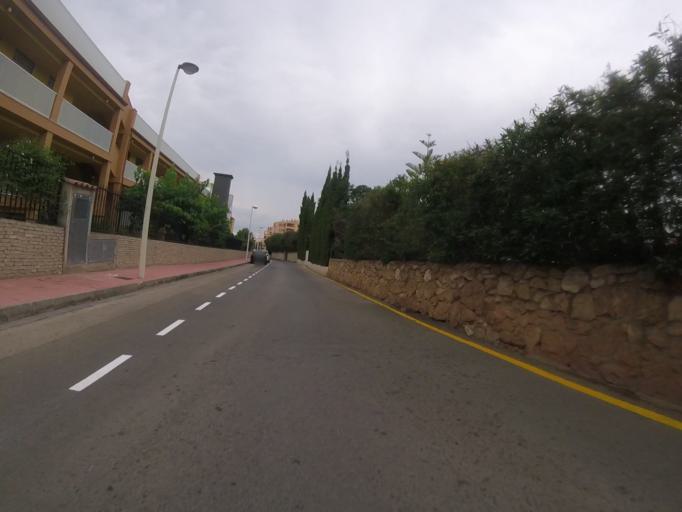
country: ES
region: Valencia
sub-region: Provincia de Castello
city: Alcoceber
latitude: 40.2579
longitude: 0.2889
